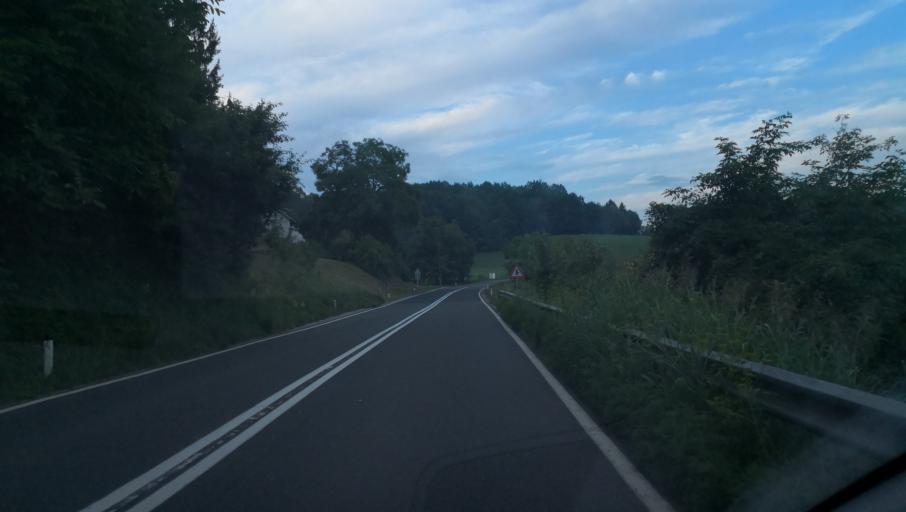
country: SI
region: Metlika
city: Metlika
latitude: 45.6663
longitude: 15.2903
